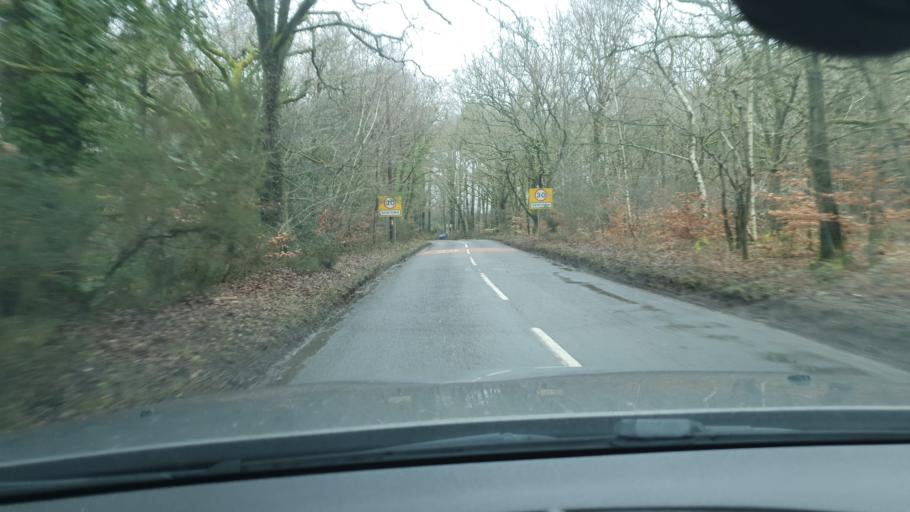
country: GB
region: England
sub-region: West Berkshire
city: Greenham
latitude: 51.3662
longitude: -1.3169
